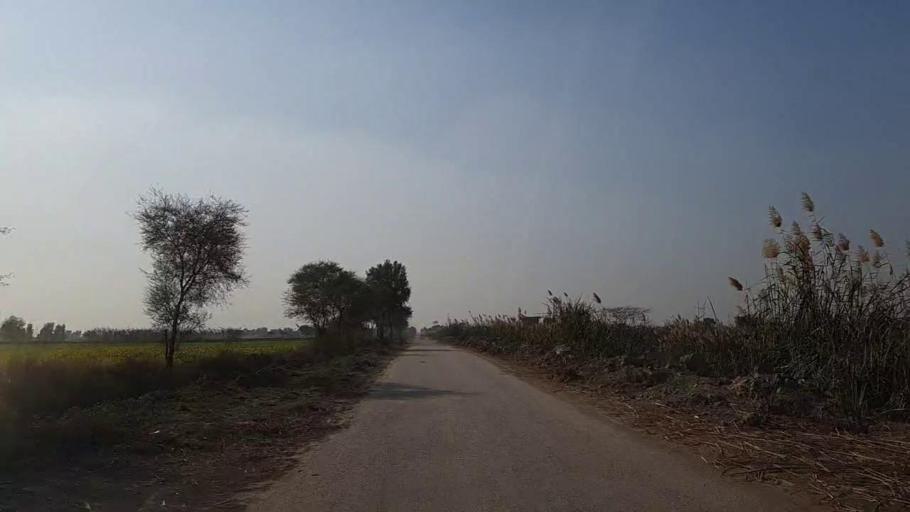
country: PK
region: Sindh
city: Daur
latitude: 26.4042
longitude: 68.2700
